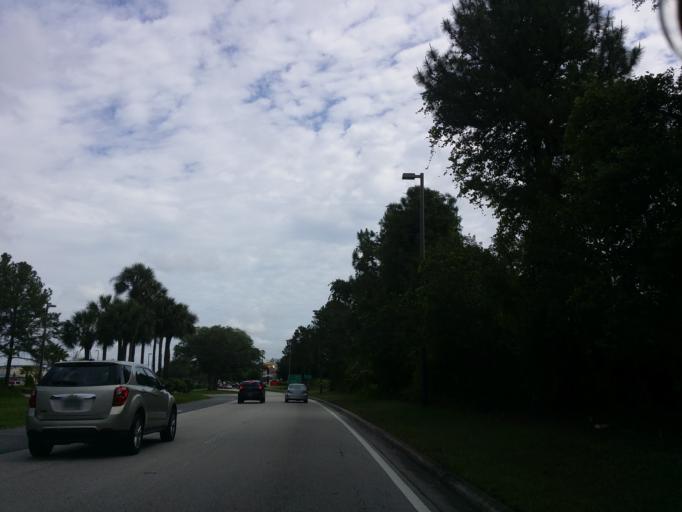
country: US
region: Florida
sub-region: Orange County
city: Williamsburg
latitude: 28.4031
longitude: -81.4568
